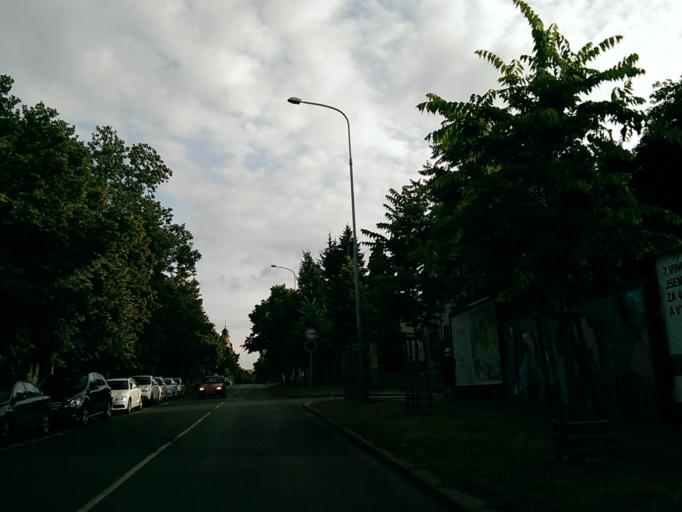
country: CZ
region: Praha
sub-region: Praha 8
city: Karlin
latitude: 50.0815
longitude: 14.4390
